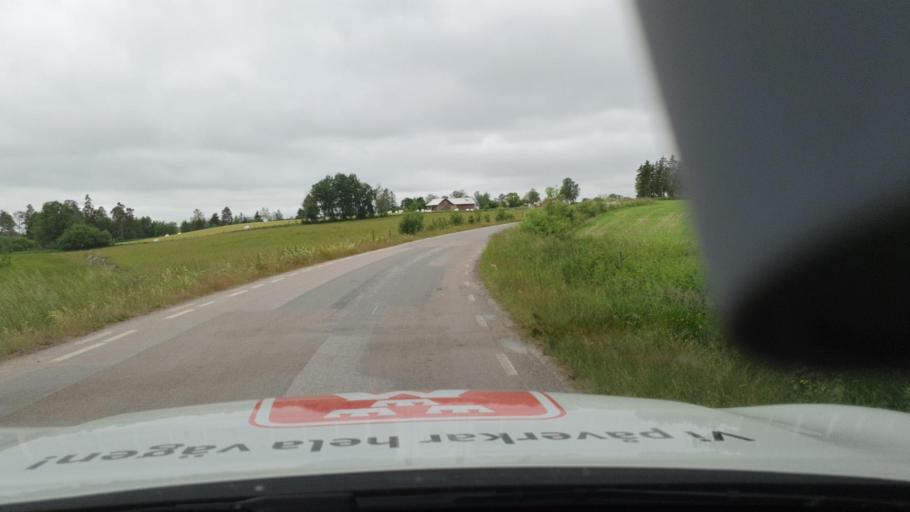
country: SE
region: Vaestra Goetaland
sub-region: Tibro Kommun
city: Tibro
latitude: 58.3976
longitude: 14.1216
